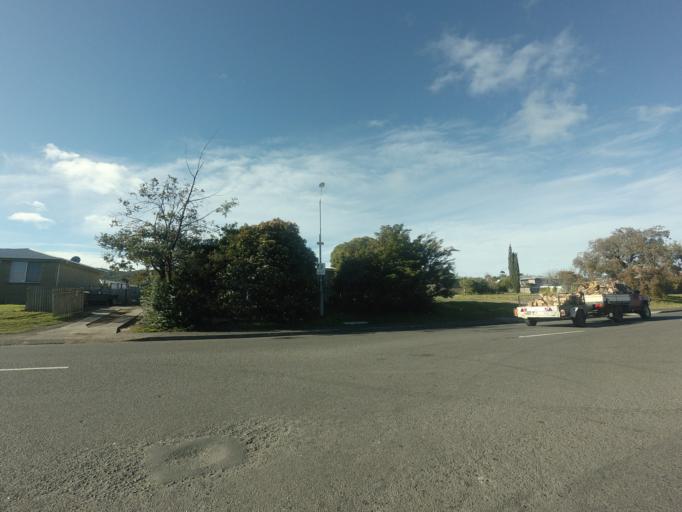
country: AU
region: Tasmania
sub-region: Clarence
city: Rokeby
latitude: -42.8892
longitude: 147.4412
